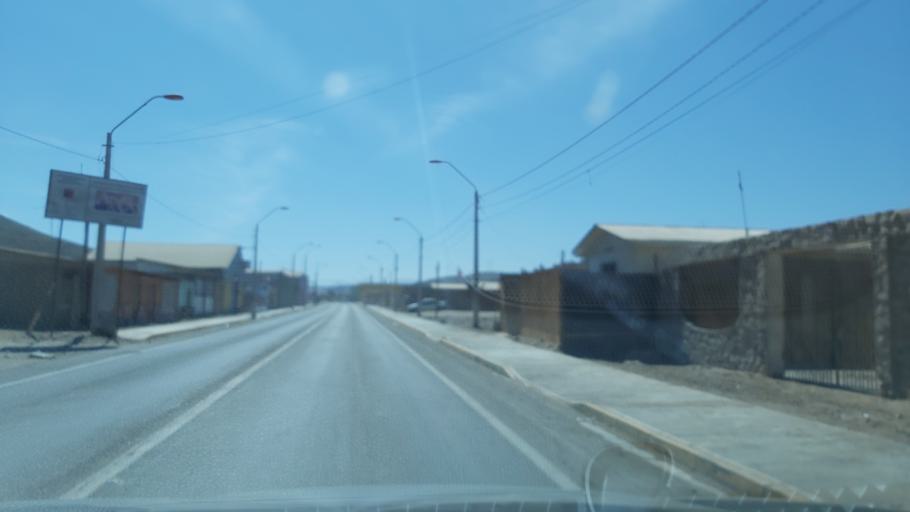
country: CL
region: Atacama
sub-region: Provincia de Chanaral
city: Diego de Almagro
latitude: -26.3911
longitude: -70.0401
